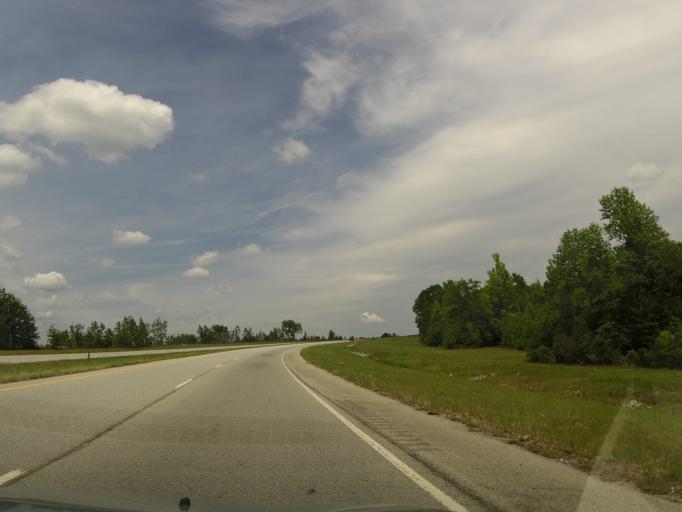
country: US
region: Georgia
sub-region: Emanuel County
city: Swainsboro
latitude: 32.6325
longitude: -82.3752
